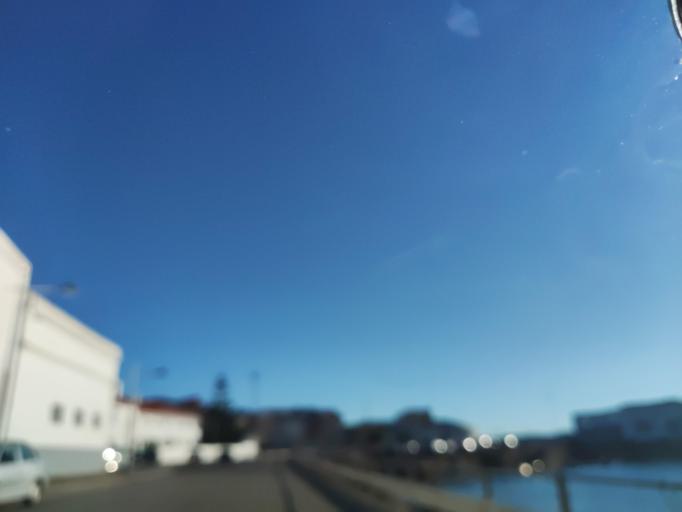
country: ES
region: Galicia
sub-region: Provincia da Coruna
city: Boiro
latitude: 42.6157
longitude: -8.8860
